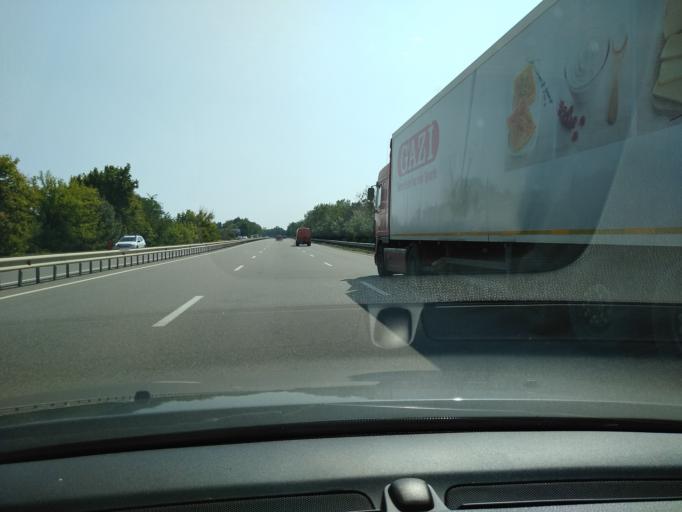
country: MD
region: Chisinau
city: Cricova
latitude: 47.1217
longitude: 28.8525
